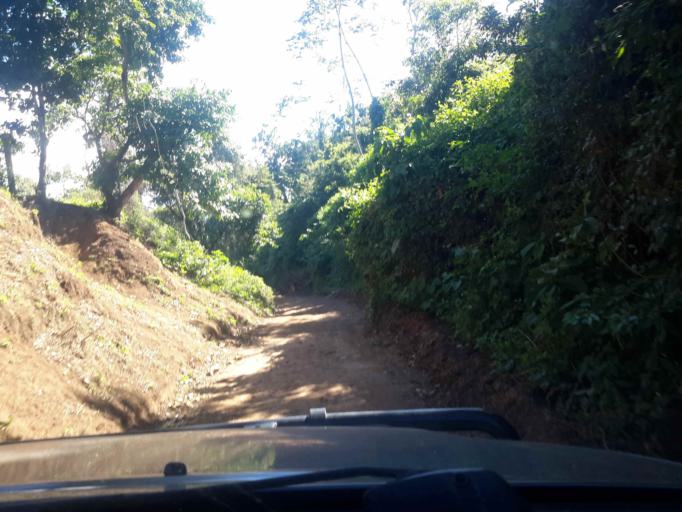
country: NI
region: Carazo
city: Jinotepe
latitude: 11.8541
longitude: -86.1739
